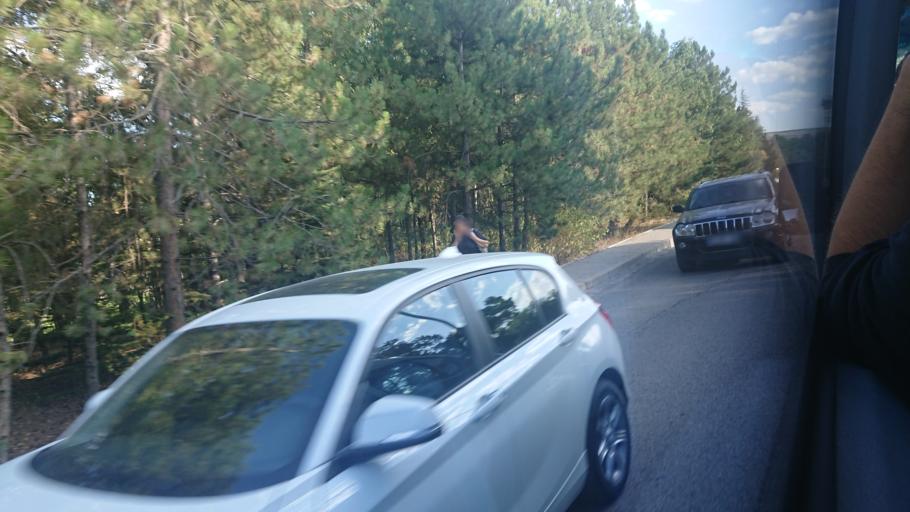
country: TR
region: Ankara
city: Ankara
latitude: 39.8919
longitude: 32.7840
